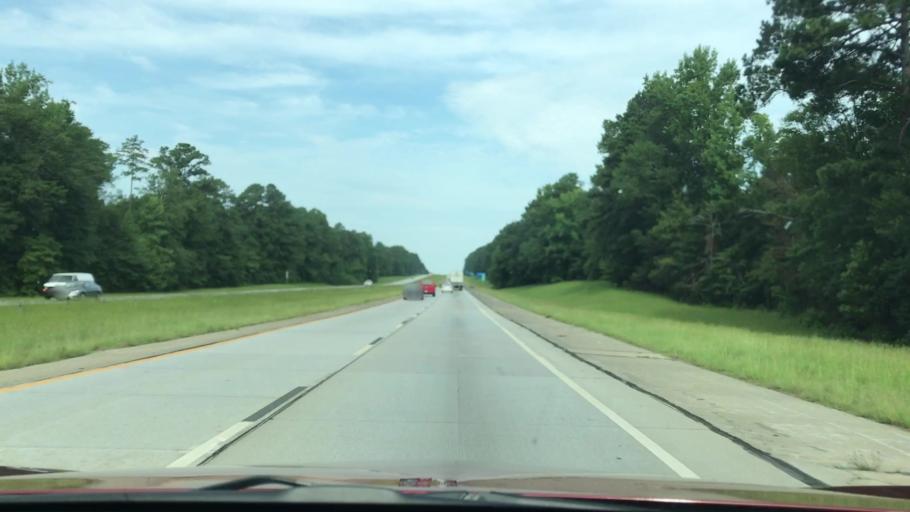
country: US
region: Georgia
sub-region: McDuffie County
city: Thomson
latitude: 33.5080
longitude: -82.4140
